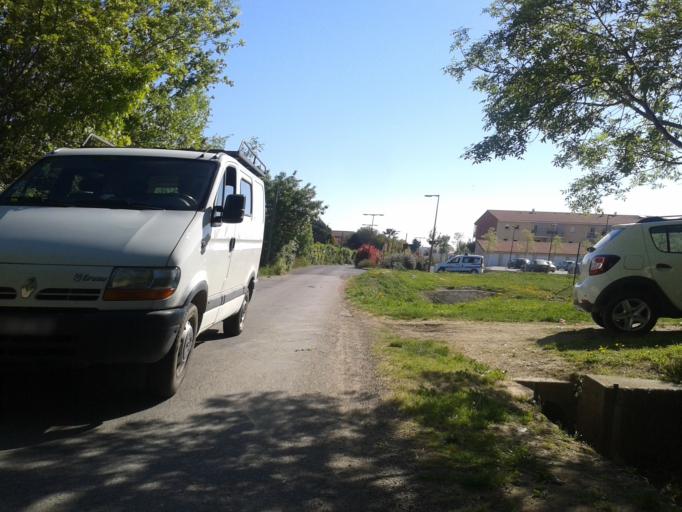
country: FR
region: Languedoc-Roussillon
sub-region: Departement des Pyrenees-Orientales
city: Toulouges
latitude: 42.6731
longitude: 2.8233
